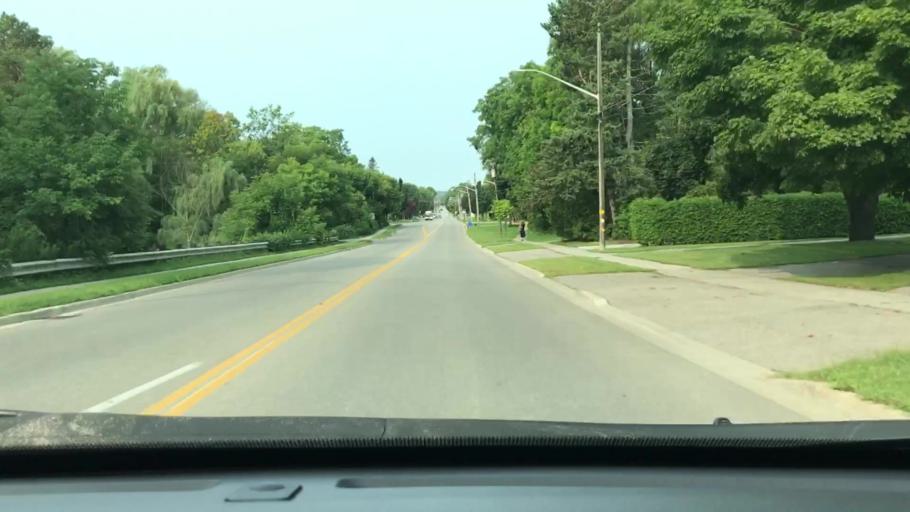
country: CA
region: Ontario
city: Newmarket
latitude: 44.0553
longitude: -79.4366
